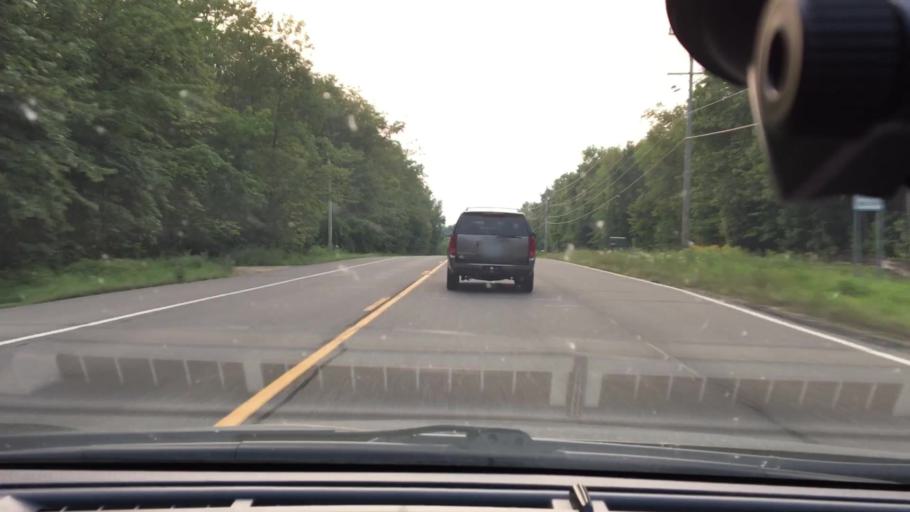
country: US
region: Minnesota
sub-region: Crow Wing County
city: Crosby
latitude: 46.4894
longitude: -93.9106
